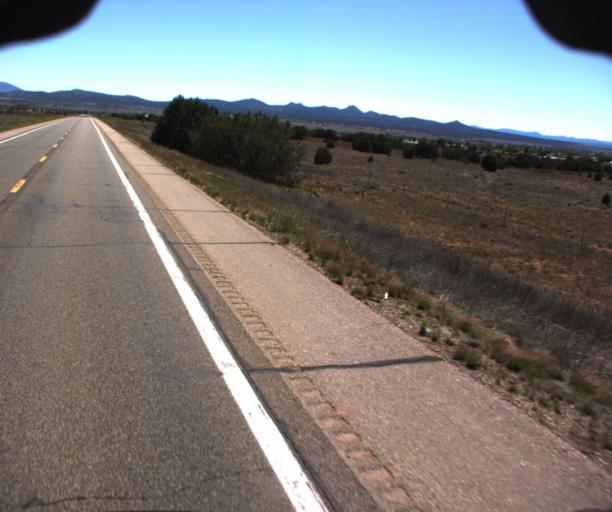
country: US
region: Arizona
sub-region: Yavapai County
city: Paulden
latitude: 34.9172
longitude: -112.4560
